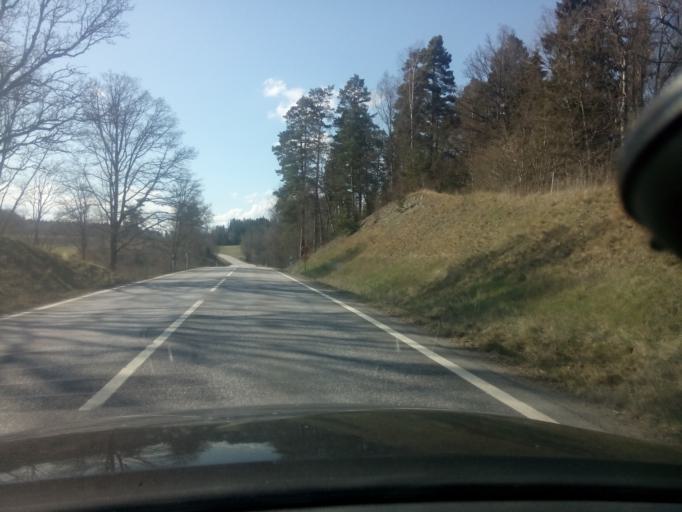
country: SE
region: Soedermanland
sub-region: Flens Kommun
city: Malmkoping
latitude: 59.1011
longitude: 16.7925
